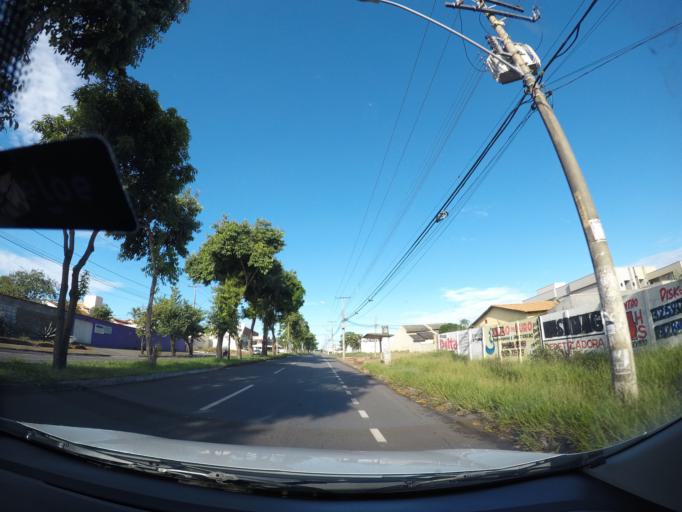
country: BR
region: Goias
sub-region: Goiania
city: Goiania
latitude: -16.7335
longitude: -49.3016
